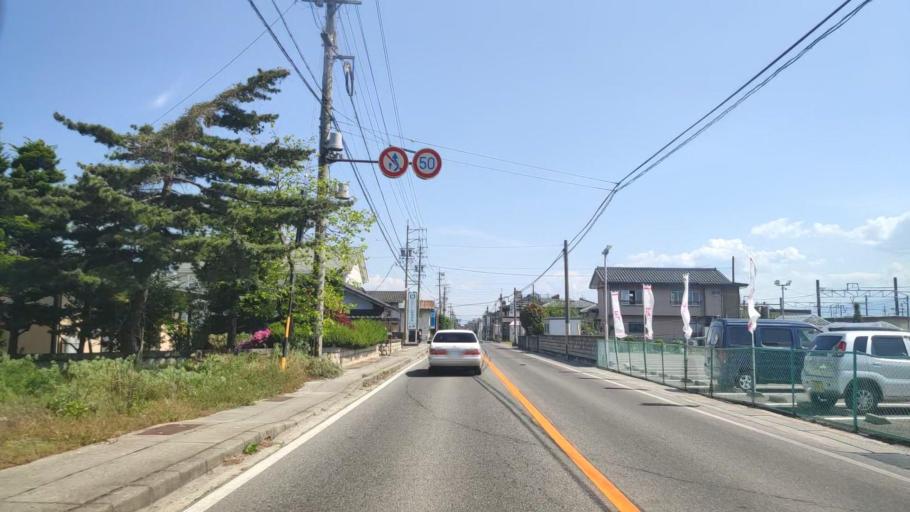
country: JP
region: Nagano
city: Hotaka
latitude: 36.3607
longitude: 137.8785
